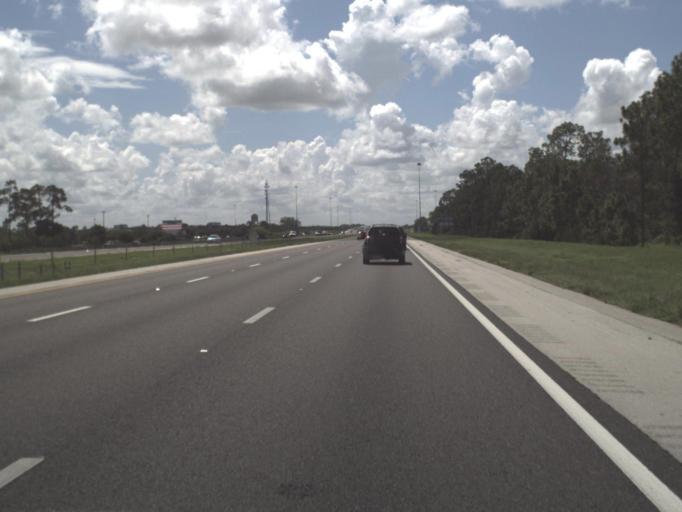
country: US
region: Florida
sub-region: Lee County
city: Estero
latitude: 26.4425
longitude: -81.7818
